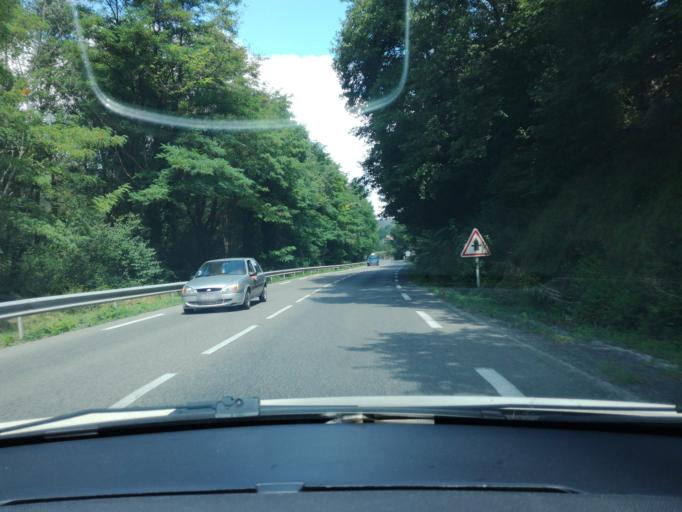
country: FR
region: Rhone-Alpes
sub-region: Departement de l'Ardeche
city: Ruoms
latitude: 44.4827
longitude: 4.3796
